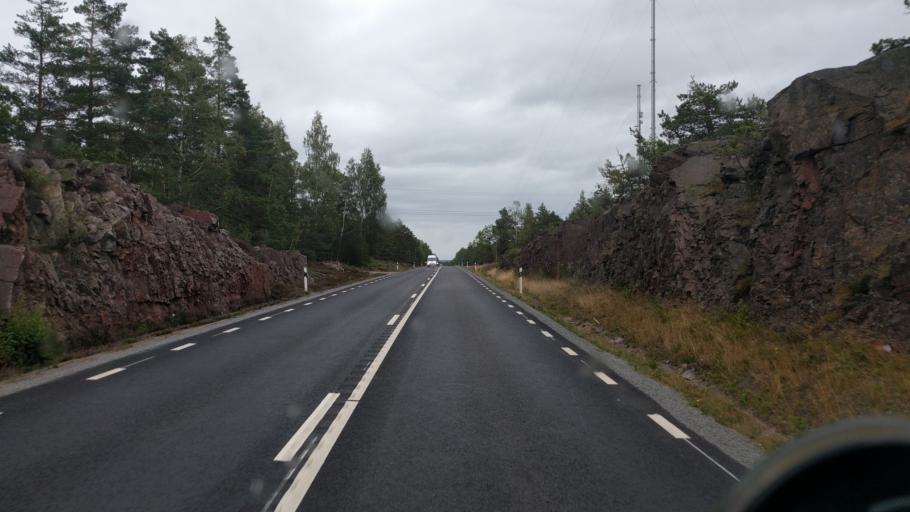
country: SE
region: Kalmar
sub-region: Vasterviks Kommun
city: Ankarsrum
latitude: 57.7232
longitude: 16.4179
